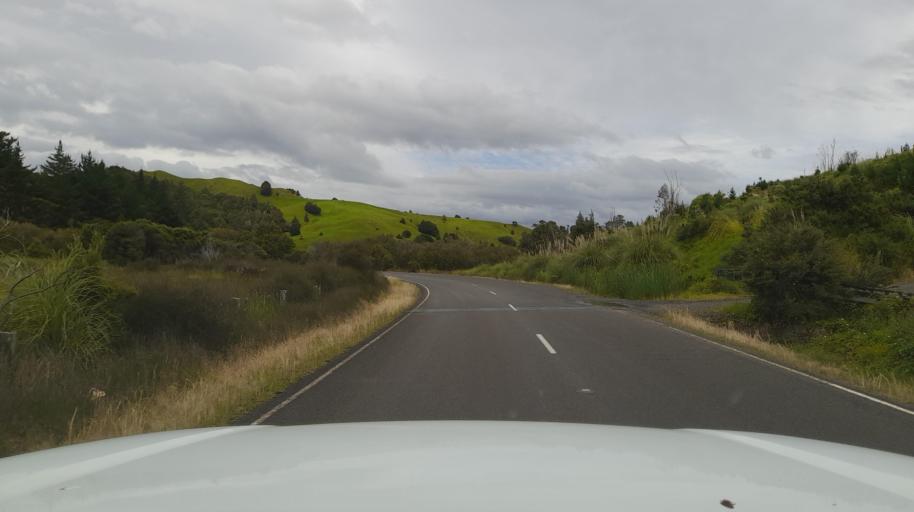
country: NZ
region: Northland
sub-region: Far North District
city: Kaitaia
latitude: -35.3613
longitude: 173.4692
